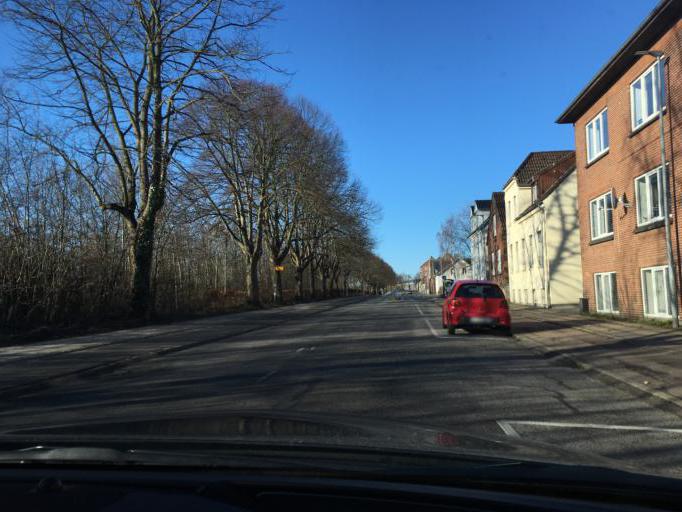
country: DK
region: South Denmark
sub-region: Kolding Kommune
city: Kolding
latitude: 55.4947
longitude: 9.4890
